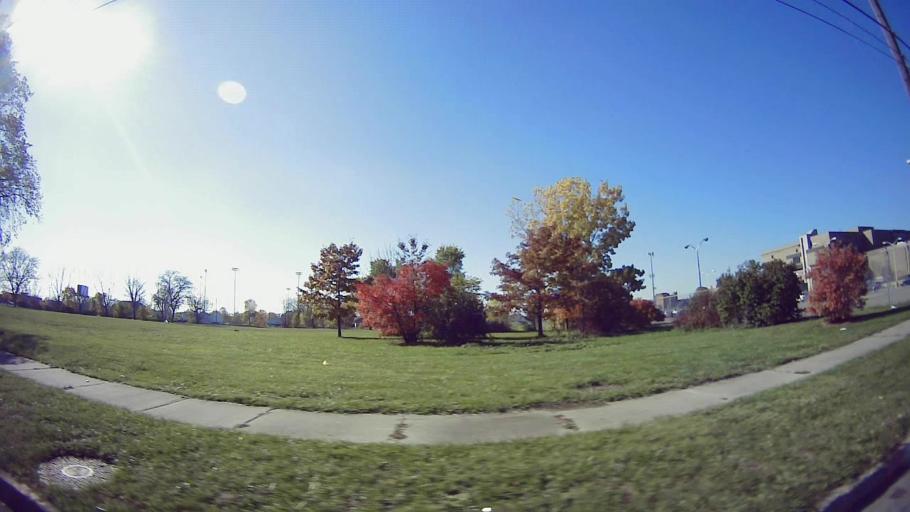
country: US
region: Michigan
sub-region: Wayne County
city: Highland Park
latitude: 42.3572
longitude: -83.1008
